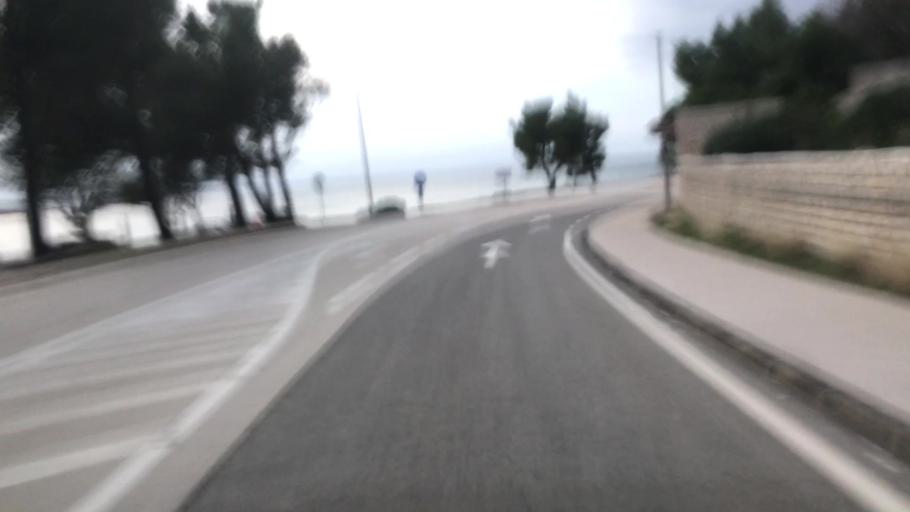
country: HR
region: Zadarska
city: Starigrad
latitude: 44.2887
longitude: 15.4459
